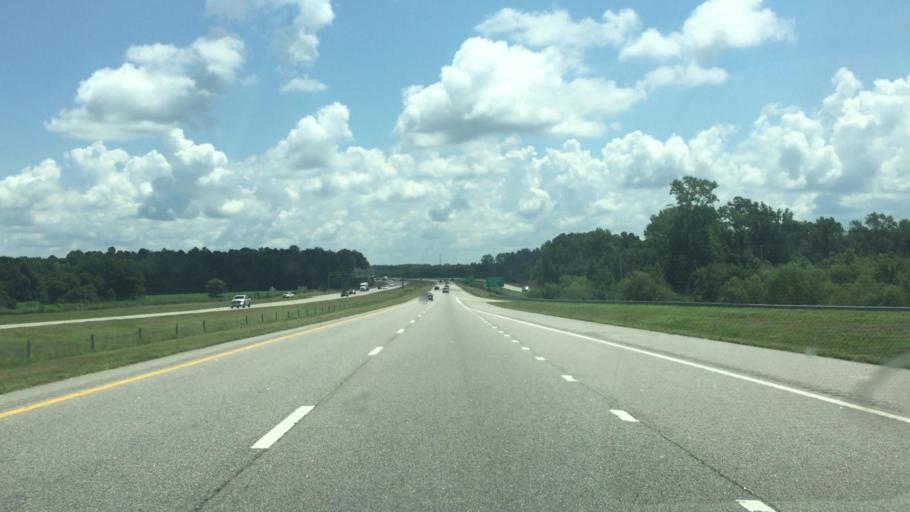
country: US
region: North Carolina
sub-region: Robeson County
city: Fairmont
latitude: 34.5925
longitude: -79.1075
